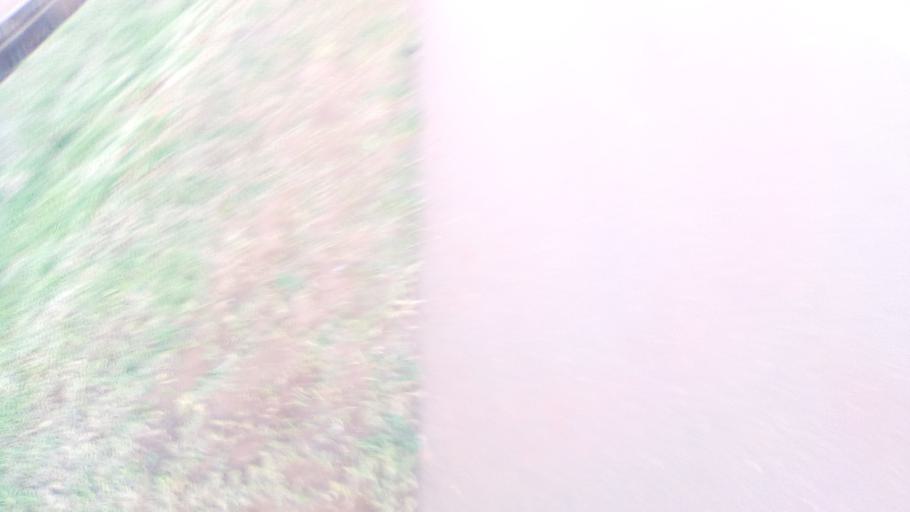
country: UG
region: Central Region
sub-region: Wakiso District
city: Entebbe
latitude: 0.0964
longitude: 32.5037
